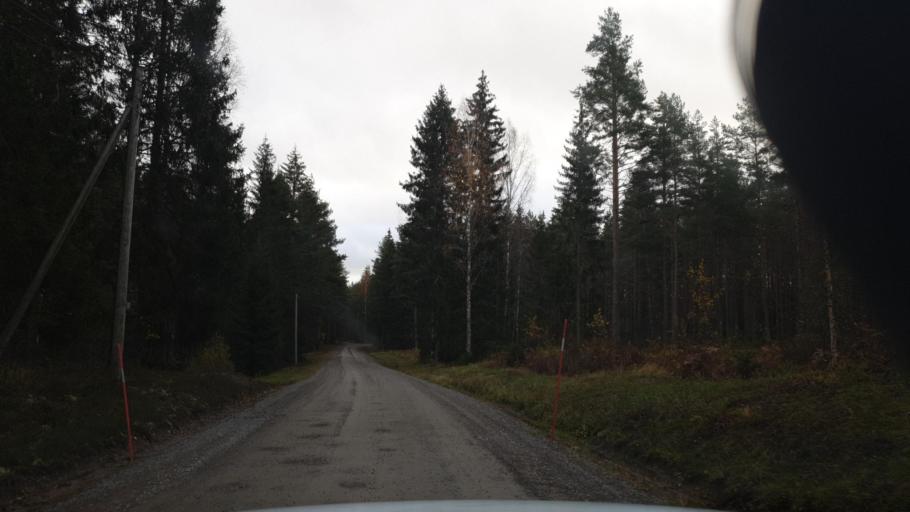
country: SE
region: Vaermland
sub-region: Arvika Kommun
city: Arvika
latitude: 59.5197
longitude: 12.7339
